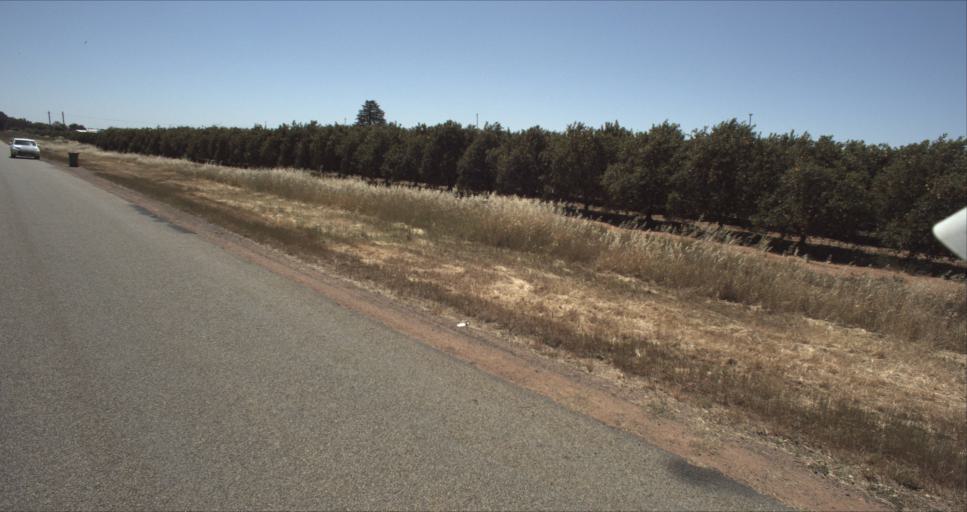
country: AU
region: New South Wales
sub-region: Leeton
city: Leeton
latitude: -34.5438
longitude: 146.3661
